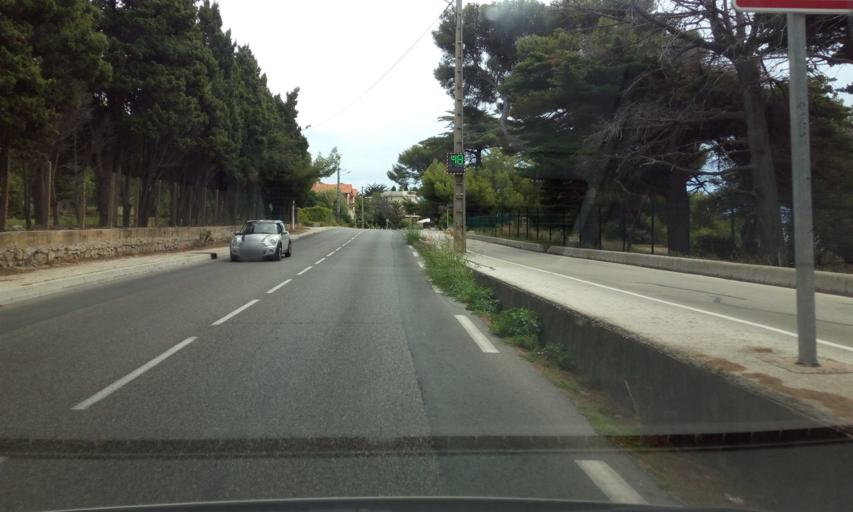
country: FR
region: Provence-Alpes-Cote d'Azur
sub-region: Departement du Var
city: Hyeres
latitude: 43.0831
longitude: 6.1169
